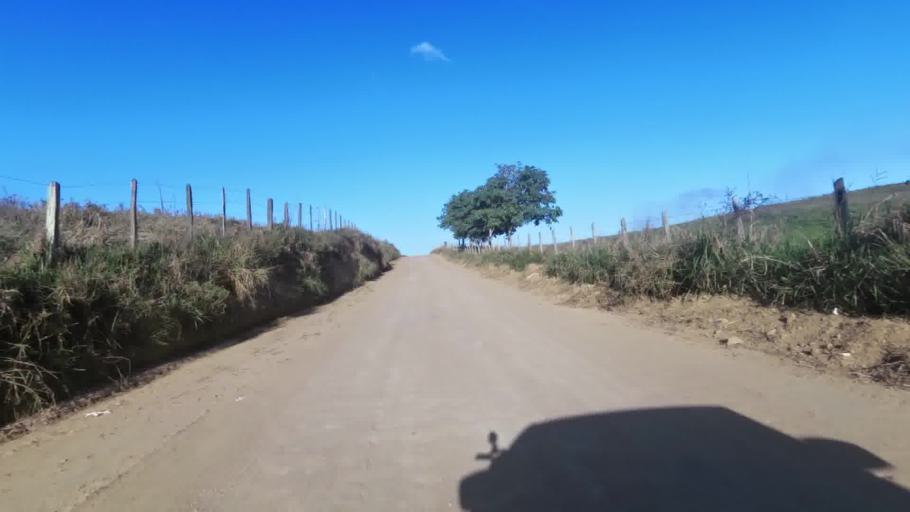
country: BR
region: Espirito Santo
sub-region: Marataizes
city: Marataizes
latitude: -21.1319
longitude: -41.0136
